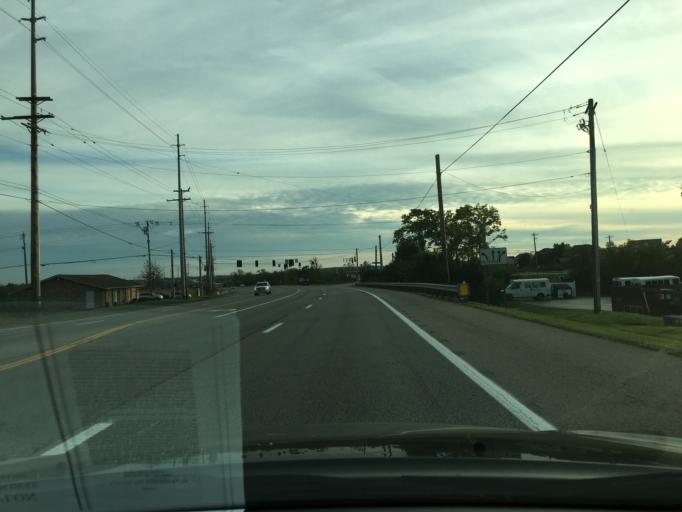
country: US
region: Ohio
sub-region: Butler County
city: Beckett Ridge
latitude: 39.3639
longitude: -84.4596
